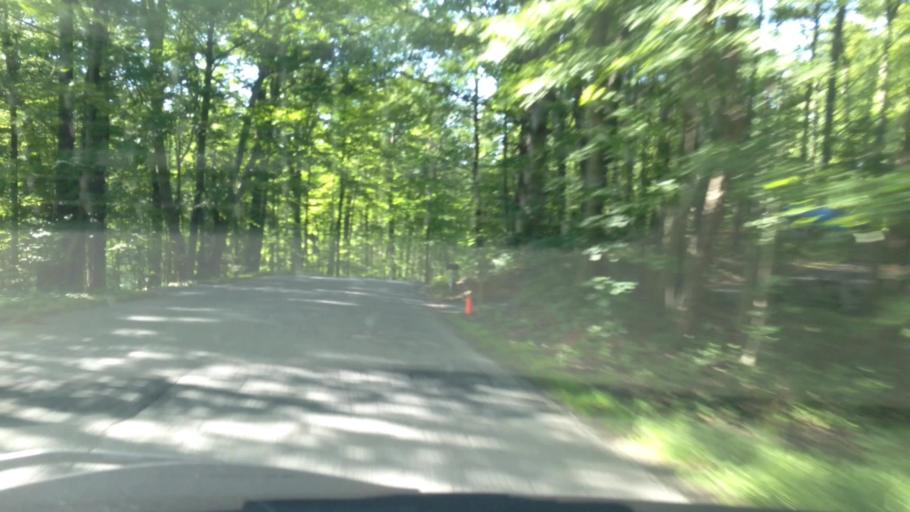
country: US
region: New York
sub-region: Ulster County
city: Tillson
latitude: 41.8147
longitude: -74.0441
